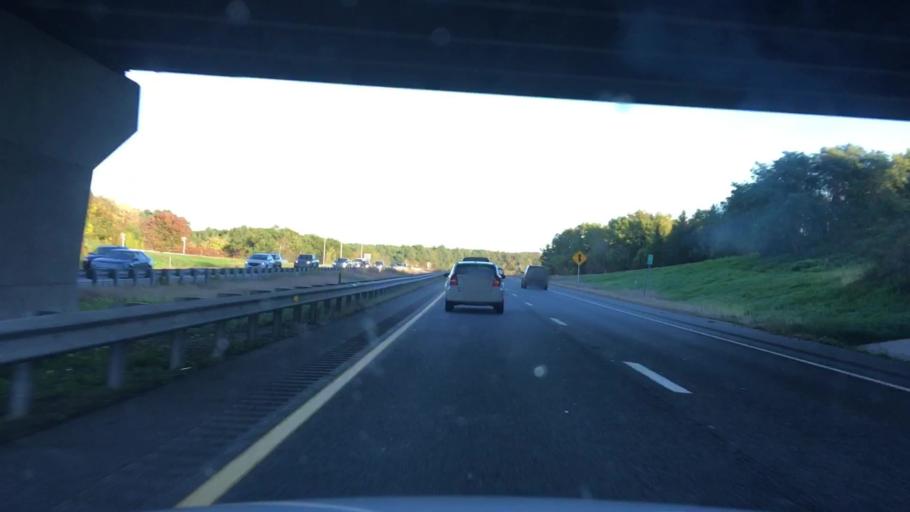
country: US
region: New Hampshire
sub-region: Rockingham County
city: Exeter
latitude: 43.0013
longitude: -70.9470
